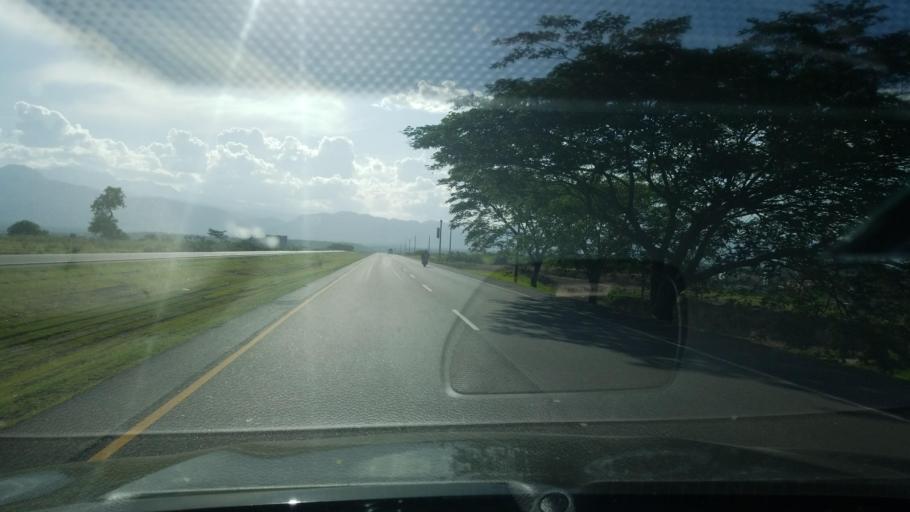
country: HN
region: Comayagua
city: Comayagua
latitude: 14.4251
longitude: -87.6341
